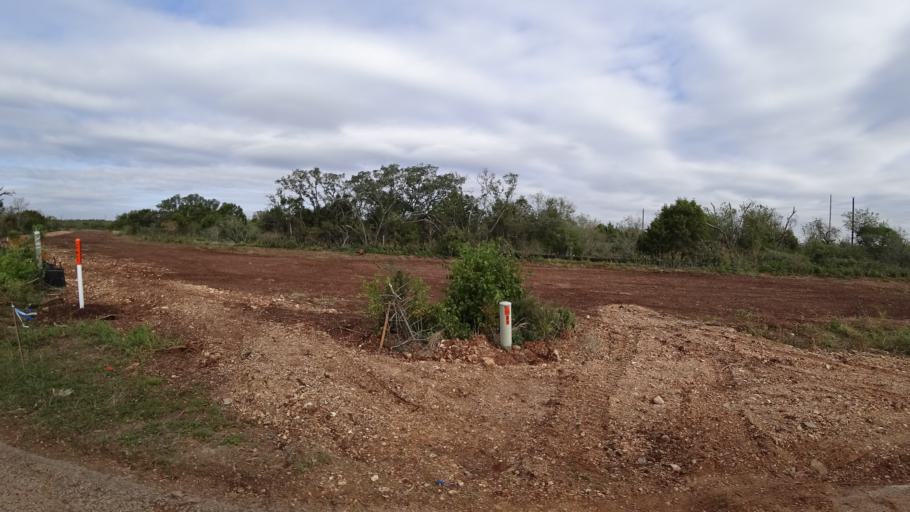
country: US
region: Texas
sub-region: Travis County
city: Shady Hollow
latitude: 30.1368
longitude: -97.8665
